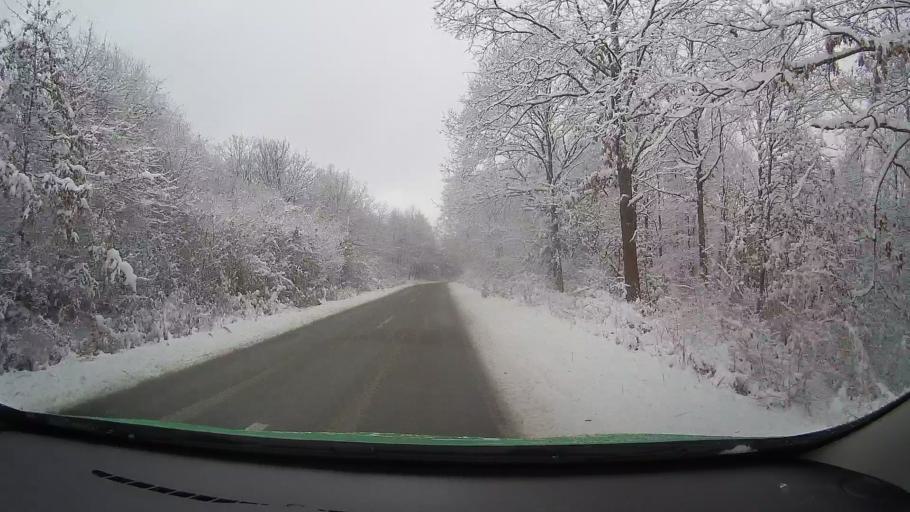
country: RO
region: Hunedoara
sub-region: Comuna Teliucu Inferior
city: Teliucu Inferior
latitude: 45.6750
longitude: 22.9143
